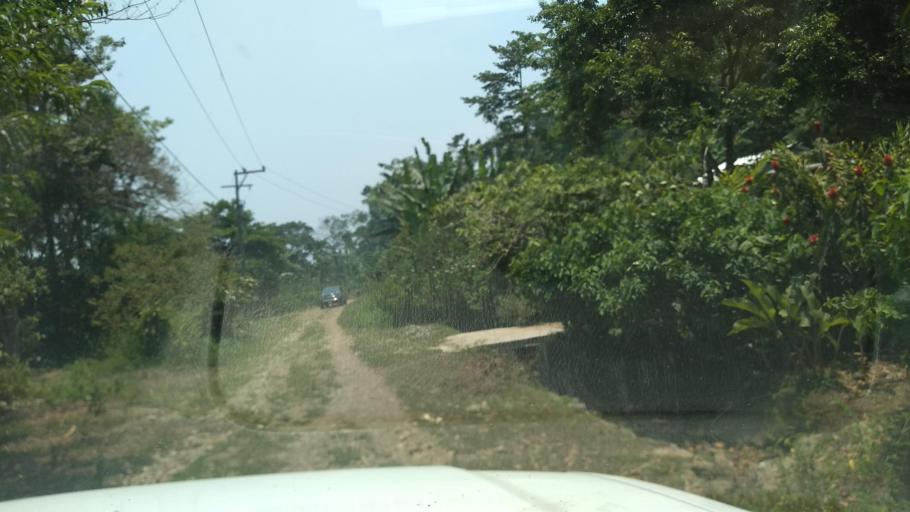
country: MX
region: Veracruz
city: Motzorongo
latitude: 18.6047
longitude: -96.7544
